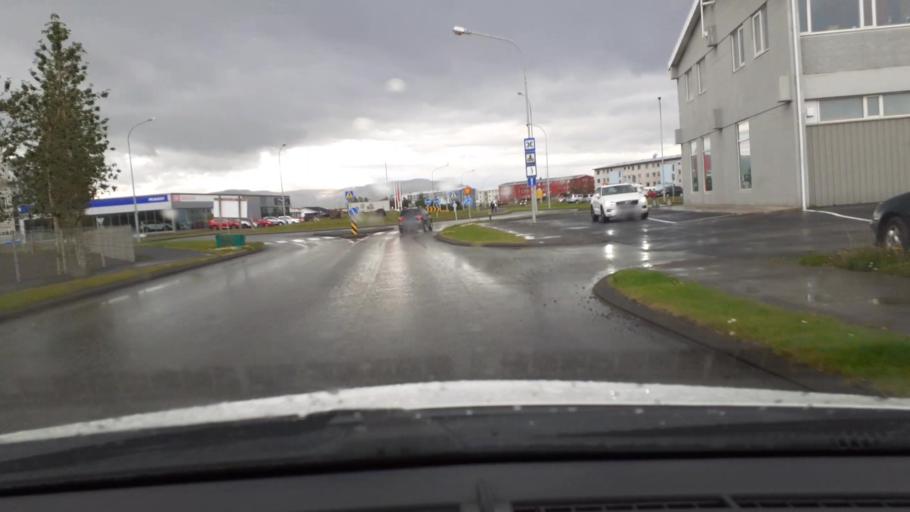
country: IS
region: West
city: Akranes
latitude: 64.3230
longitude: -22.0641
